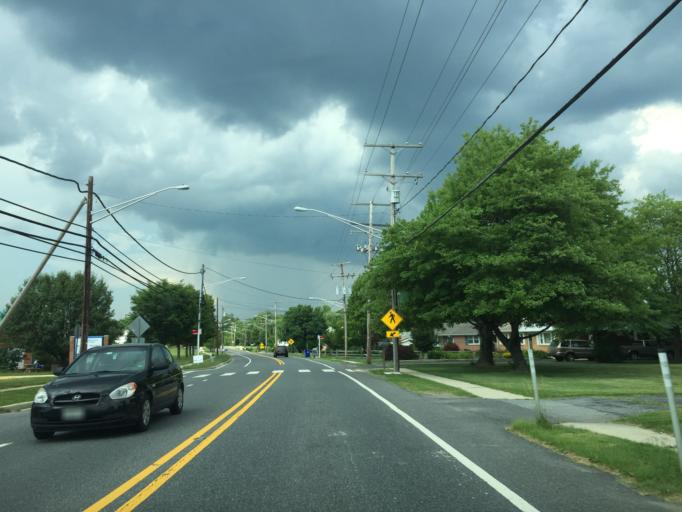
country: US
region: Maryland
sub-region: Montgomery County
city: Burtonsville
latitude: 39.1013
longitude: -76.9408
